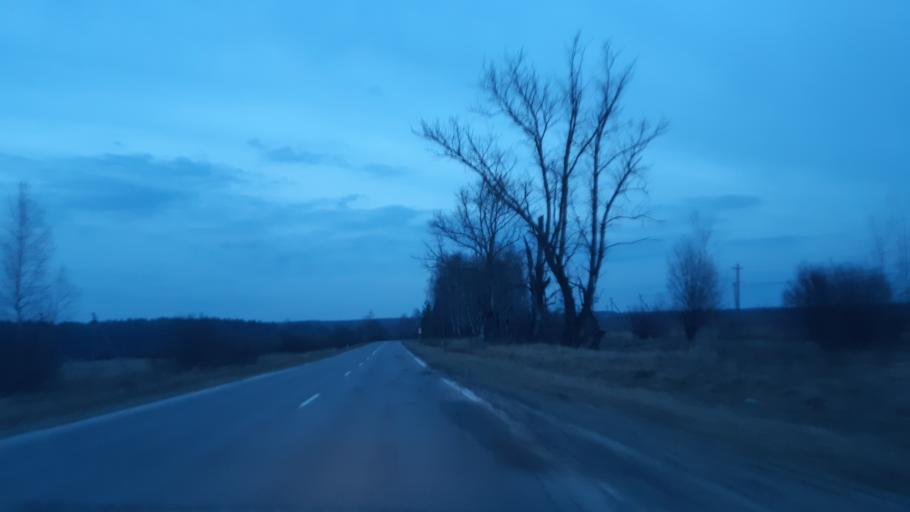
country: RU
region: Vladimir
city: Nikologory
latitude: 56.1712
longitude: 42.0009
